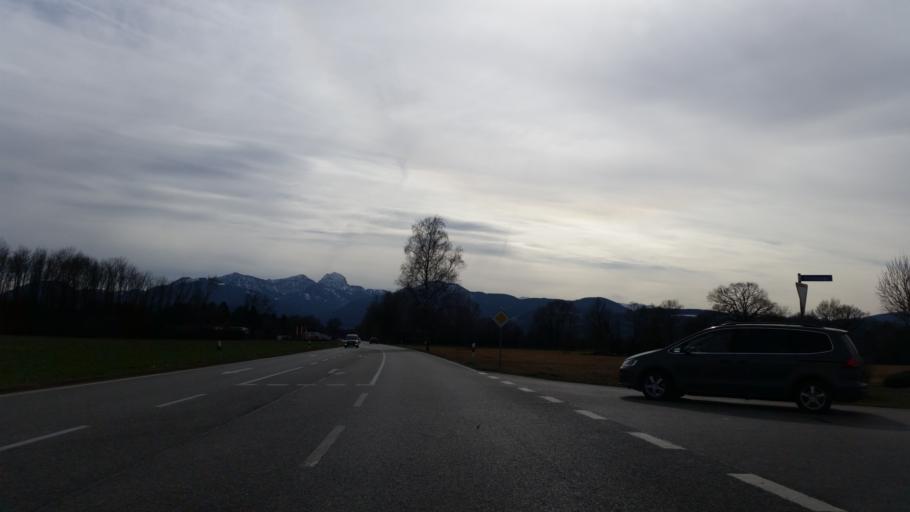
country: DE
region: Bavaria
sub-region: Upper Bavaria
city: Bad Aibling
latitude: 47.8412
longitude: 12.0120
